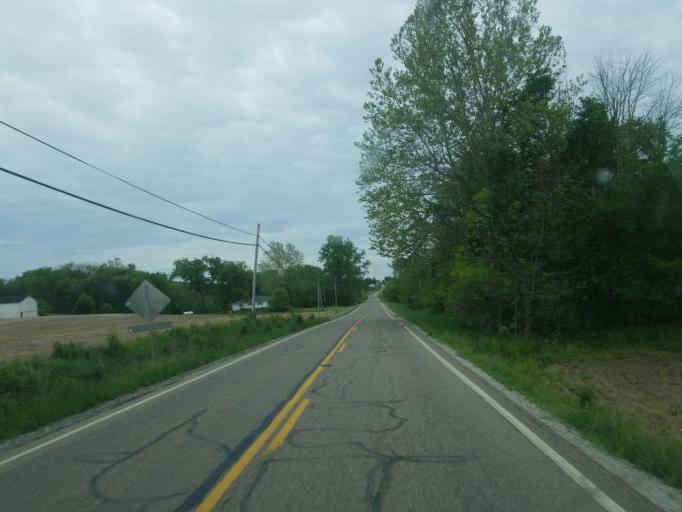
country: US
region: Ohio
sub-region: Richland County
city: Lexington
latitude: 40.6357
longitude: -82.6633
